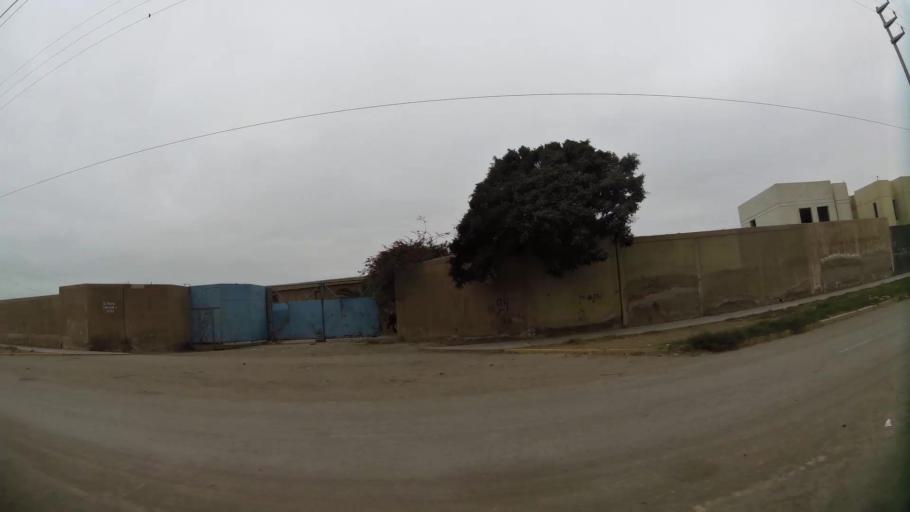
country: PE
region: Ica
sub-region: Provincia de Pisco
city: Pisco
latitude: -13.7290
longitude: -76.2016
